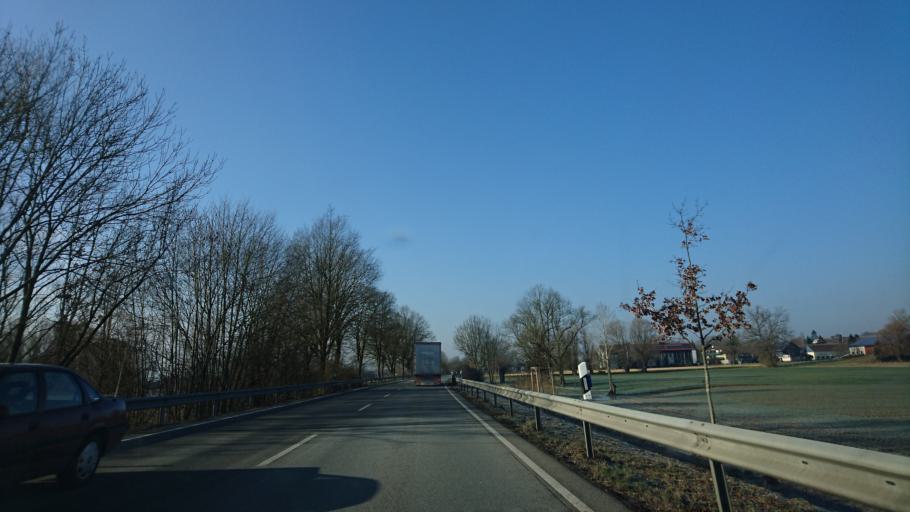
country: DE
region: Bavaria
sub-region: Lower Bavaria
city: Bad Griesbach
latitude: 48.4178
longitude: 13.1868
